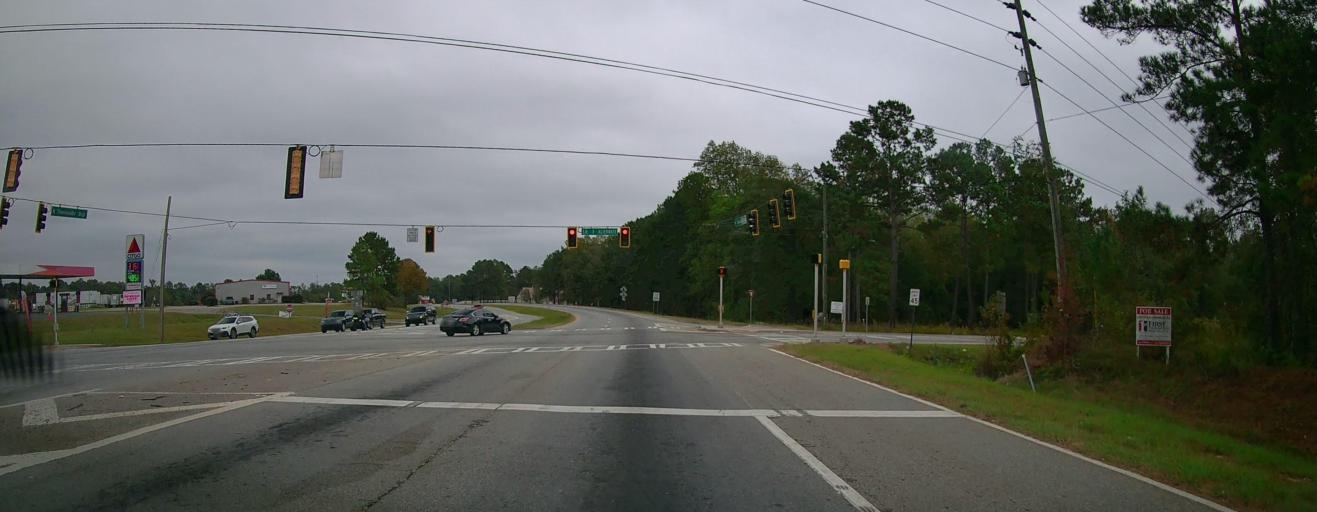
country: US
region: Georgia
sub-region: Thomas County
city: Thomasville
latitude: 30.8686
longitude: -84.0002
